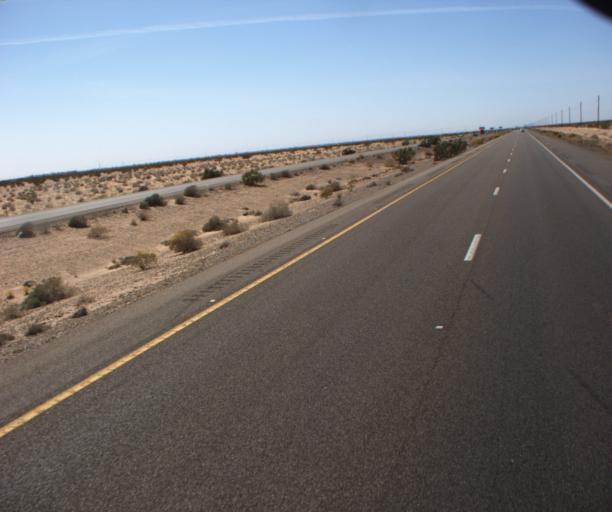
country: MX
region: Sonora
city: San Luis Rio Colorado
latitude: 32.4947
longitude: -114.6721
